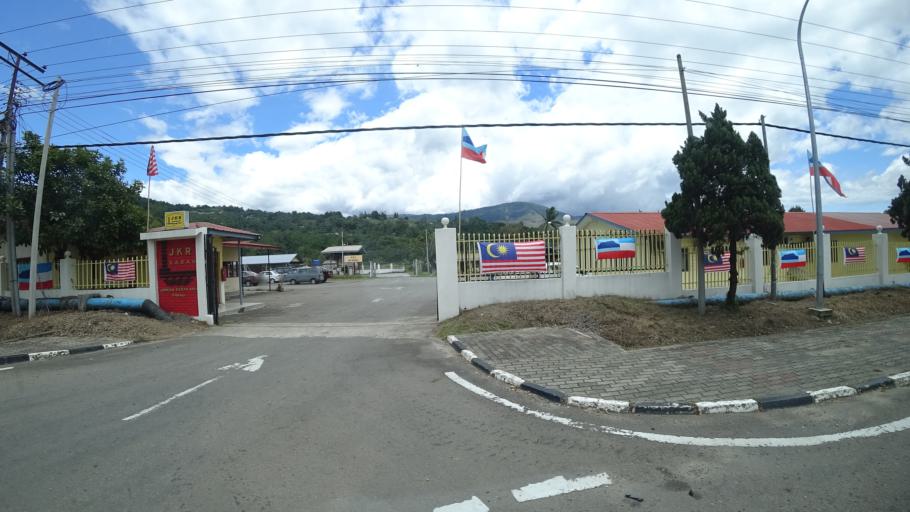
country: MY
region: Sabah
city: Ranau
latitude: 5.9546
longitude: 116.6650
